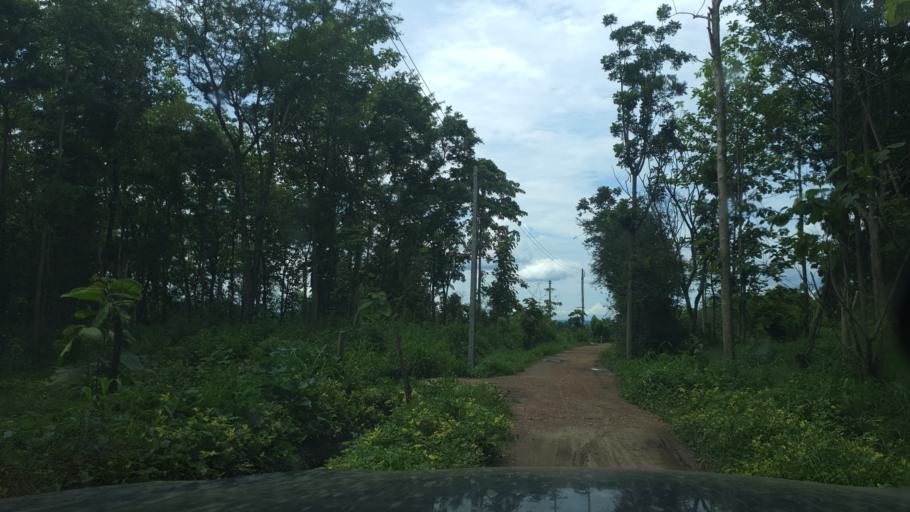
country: TH
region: Lampang
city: Sop Prap
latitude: 17.8564
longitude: 99.3961
